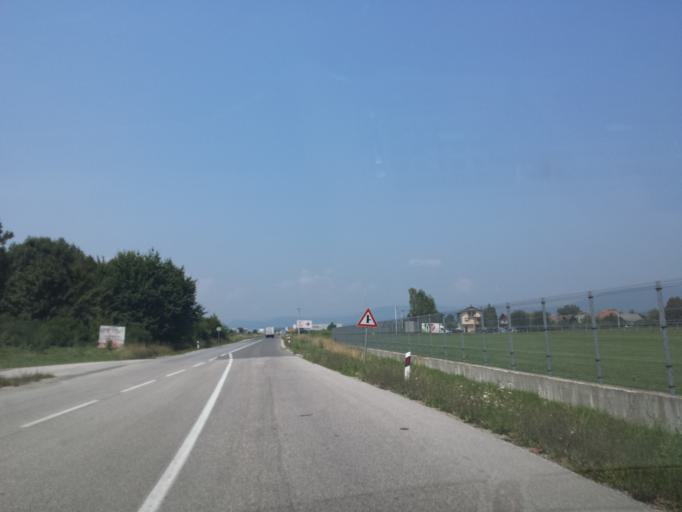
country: HR
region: Zagrebacka
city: Jastrebarsko
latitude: 45.6462
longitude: 15.6732
